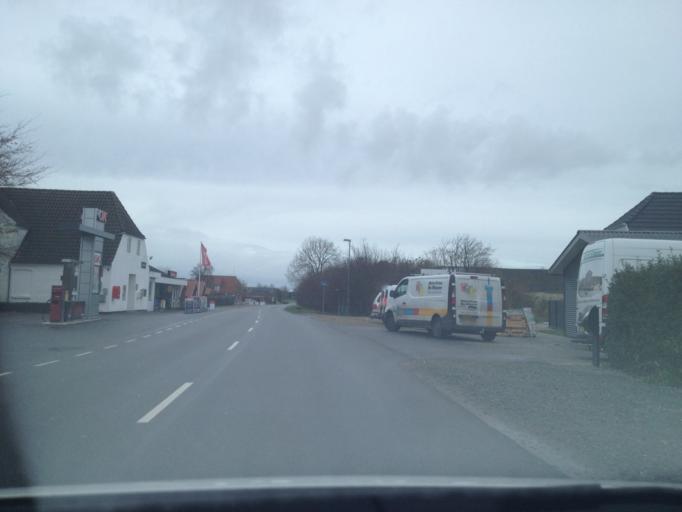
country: DK
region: South Denmark
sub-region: Esbjerg Kommune
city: Ribe
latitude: 55.2573
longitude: 8.8226
